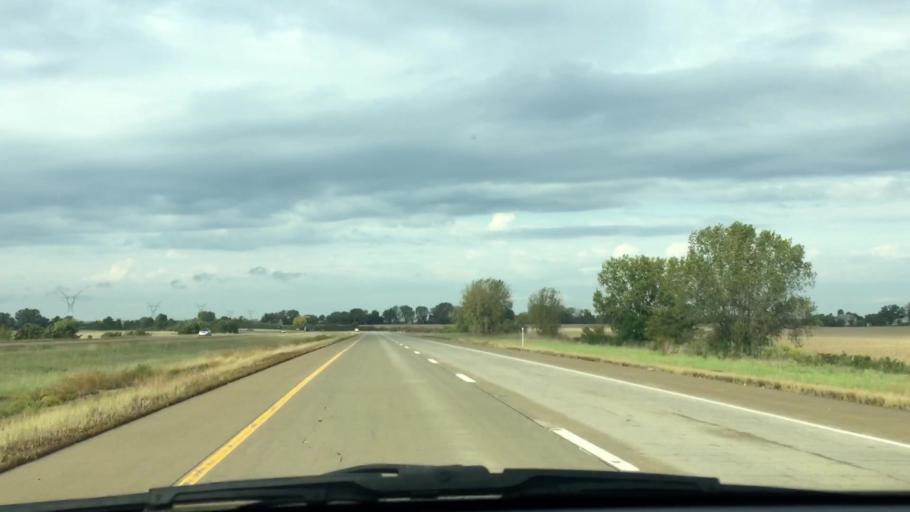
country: US
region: Illinois
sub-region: Whiteside County
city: Morrison
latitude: 41.7657
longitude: -89.8346
